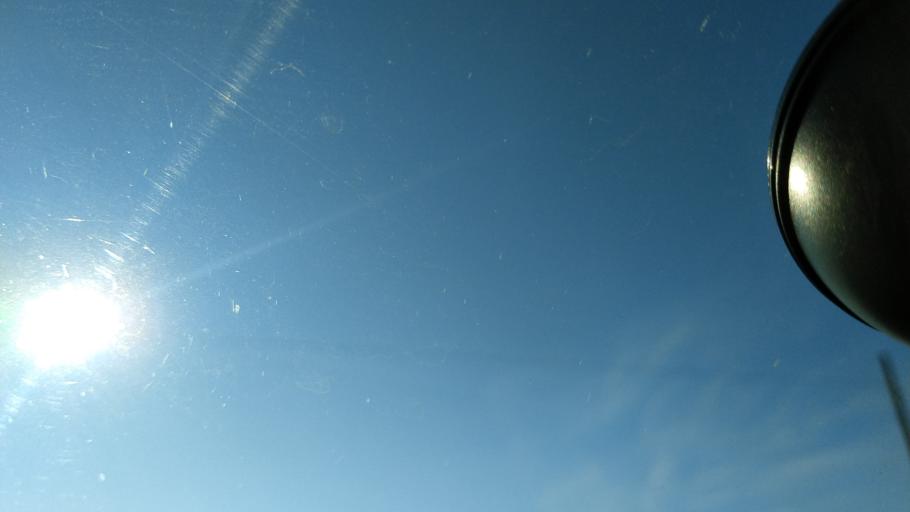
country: RO
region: Iasi
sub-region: Comuna Butea
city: Butea
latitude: 47.0764
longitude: 26.8954
